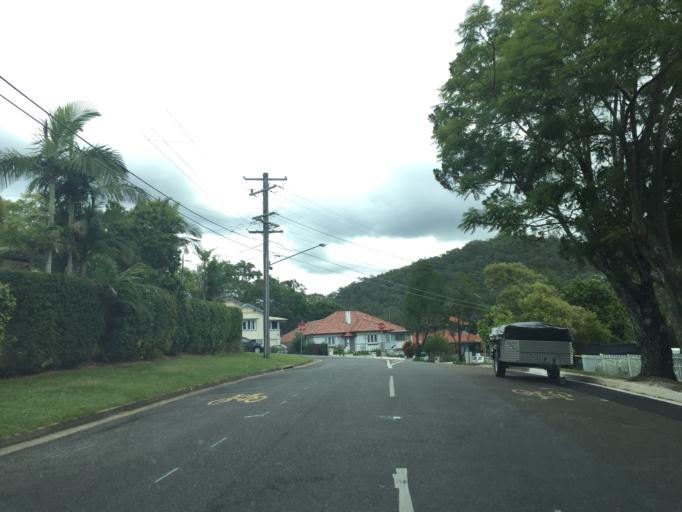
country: AU
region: Queensland
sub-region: Brisbane
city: Everton Park
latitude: -27.4427
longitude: 152.9765
